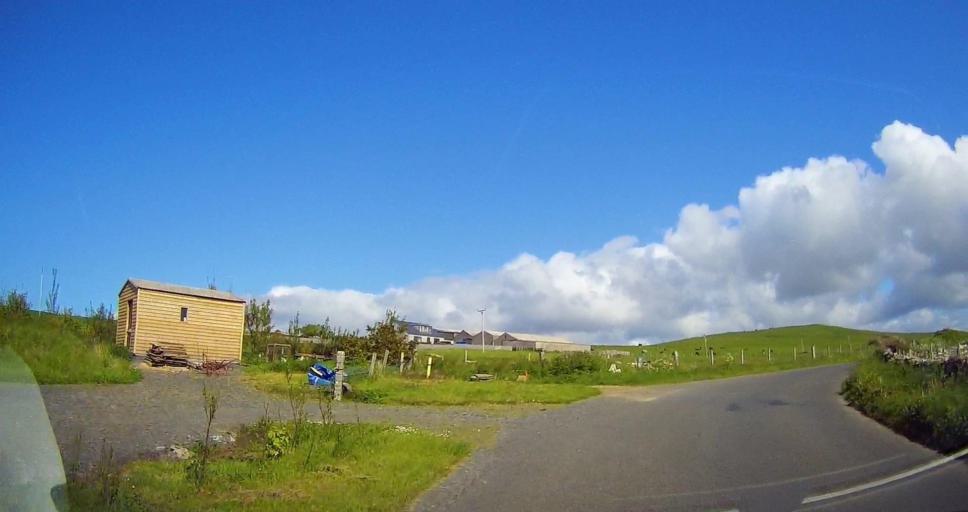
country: GB
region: Scotland
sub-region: Orkney Islands
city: Stromness
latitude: 58.9828
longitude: -3.1408
